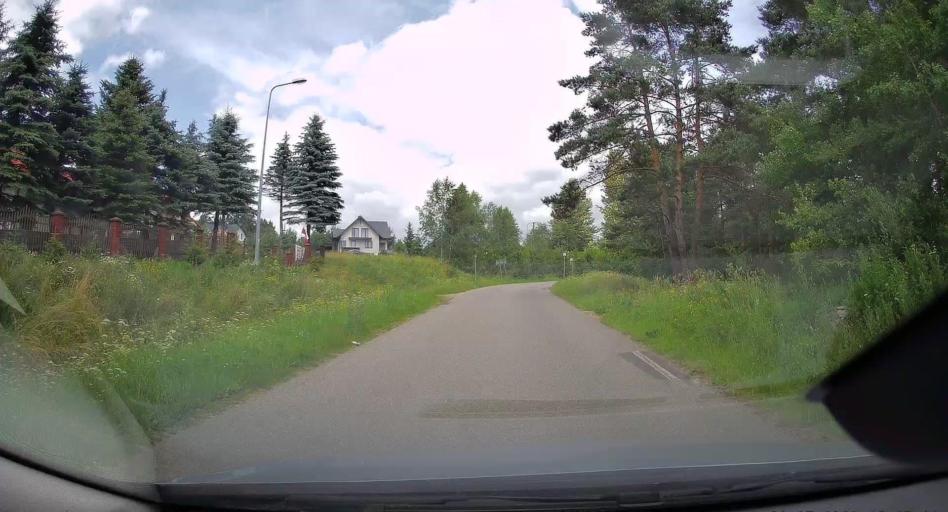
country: PL
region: Lesser Poland Voivodeship
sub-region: Powiat nowosadecki
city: Muszyna
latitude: 49.3846
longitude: 20.8998
